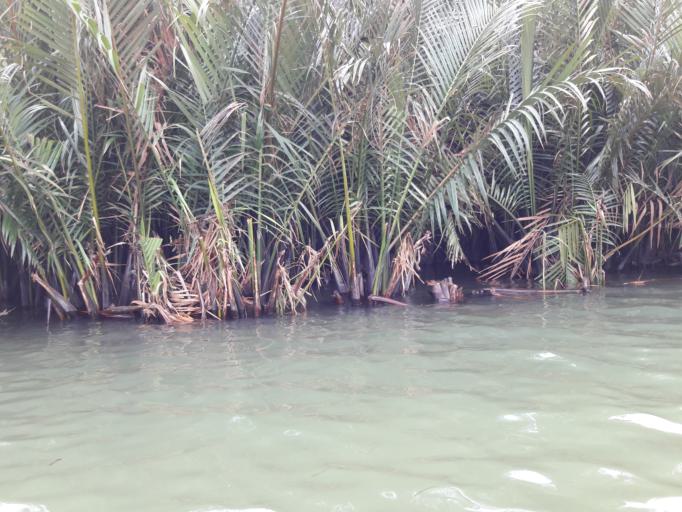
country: VN
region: Quang Nam
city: Hoi An
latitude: 15.8759
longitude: 108.3784
